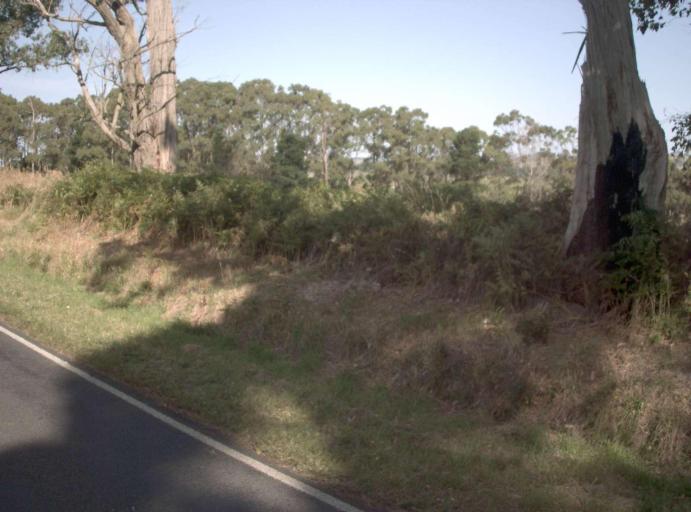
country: AU
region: Victoria
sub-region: Latrobe
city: Moe
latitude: -38.5206
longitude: 146.1109
